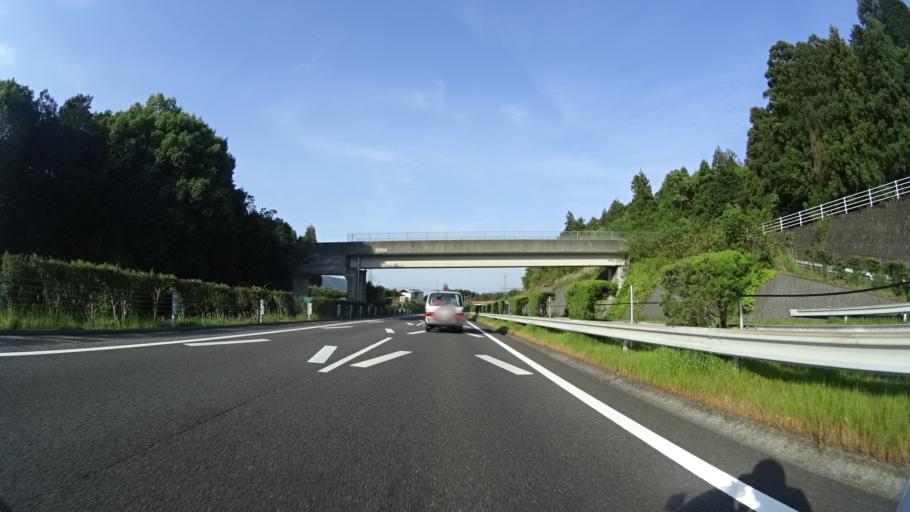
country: JP
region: Ehime
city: Niihama
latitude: 33.9383
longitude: 133.3815
